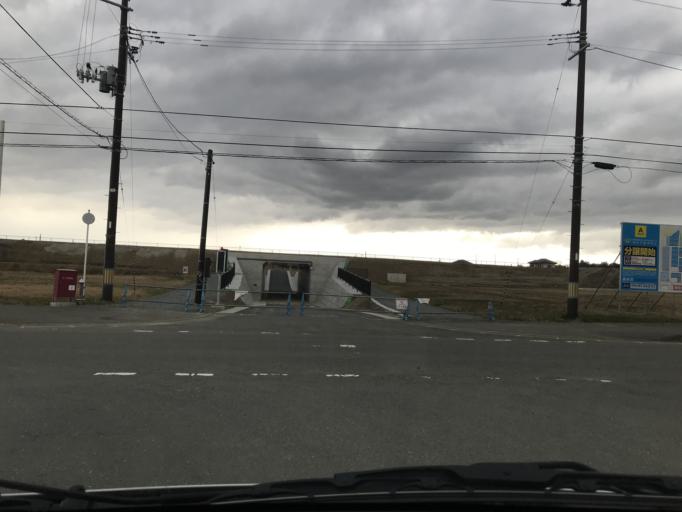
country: JP
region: Iwate
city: Mizusawa
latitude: 39.1210
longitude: 141.1625
